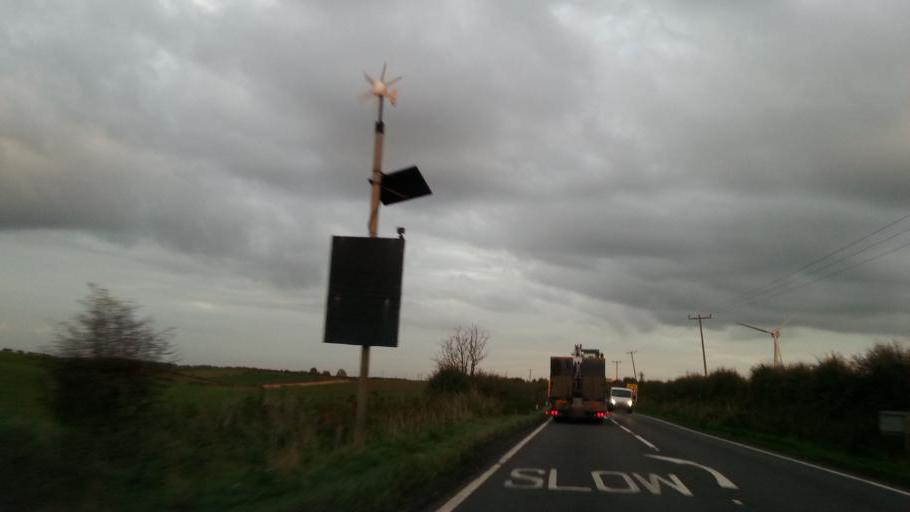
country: GB
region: England
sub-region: Nottinghamshire
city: Rainworth
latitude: 53.1180
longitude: -1.0818
